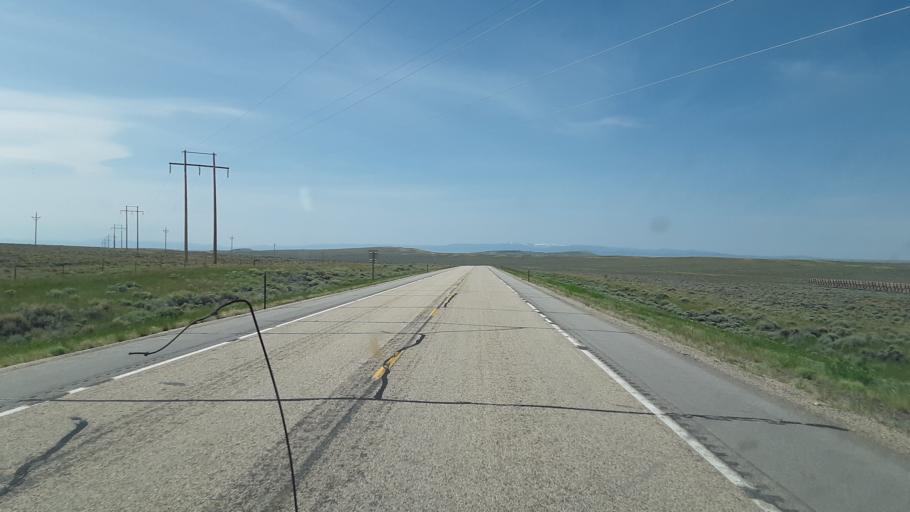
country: US
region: Wyoming
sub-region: Carbon County
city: Saratoga
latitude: 41.6135
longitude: -106.8155
